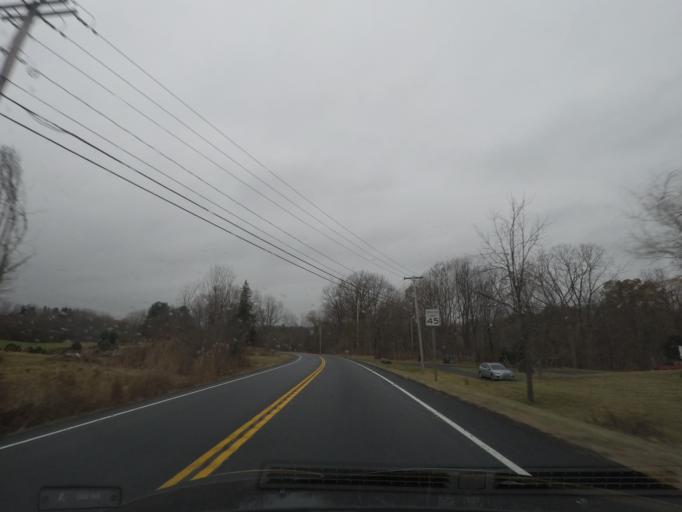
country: US
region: New York
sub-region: Rensselaer County
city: East Greenbush
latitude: 42.6211
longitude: -73.6845
